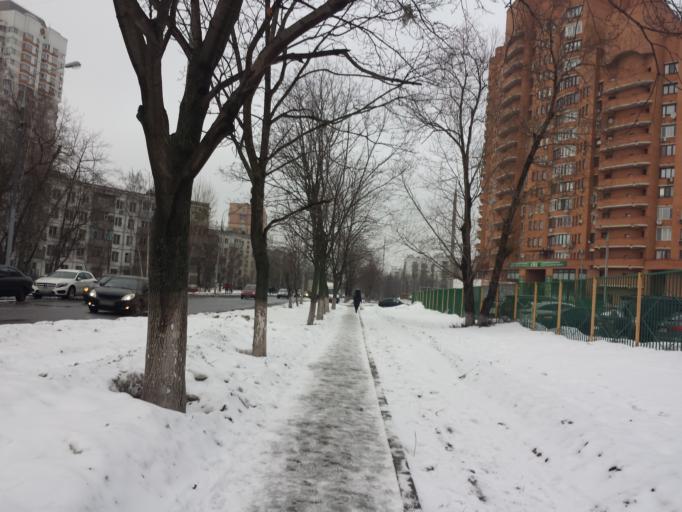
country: RU
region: Moscow
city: Novyye Kuz'minki
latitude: 55.7080
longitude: 37.7651
